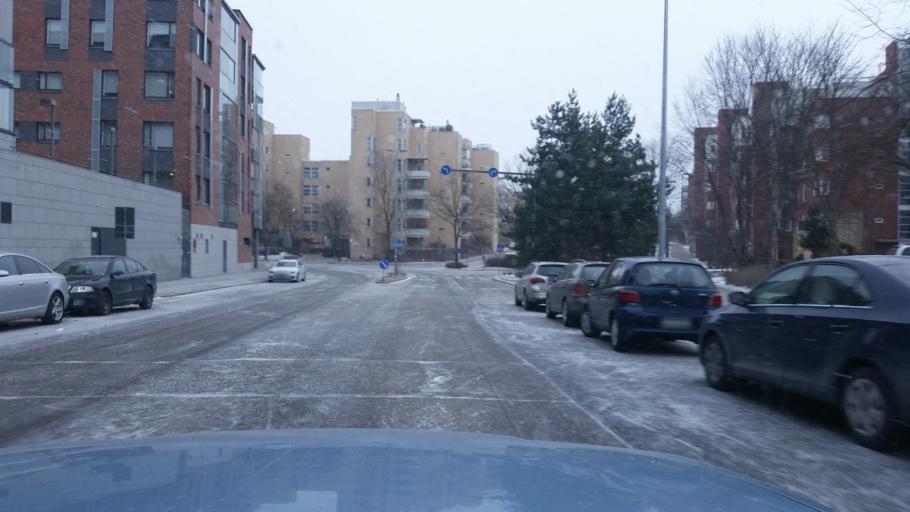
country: FI
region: Uusimaa
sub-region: Helsinki
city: Helsinki
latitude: 60.2029
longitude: 24.9197
